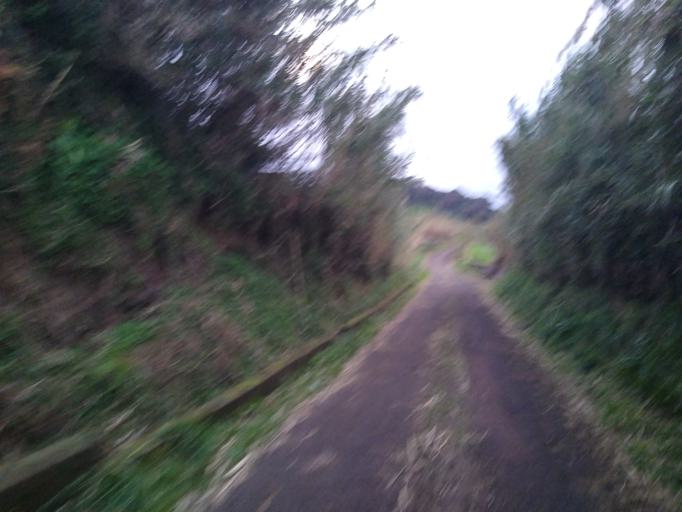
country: PT
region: Azores
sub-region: Povoacao
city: Furnas
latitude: 37.8254
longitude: -25.4069
